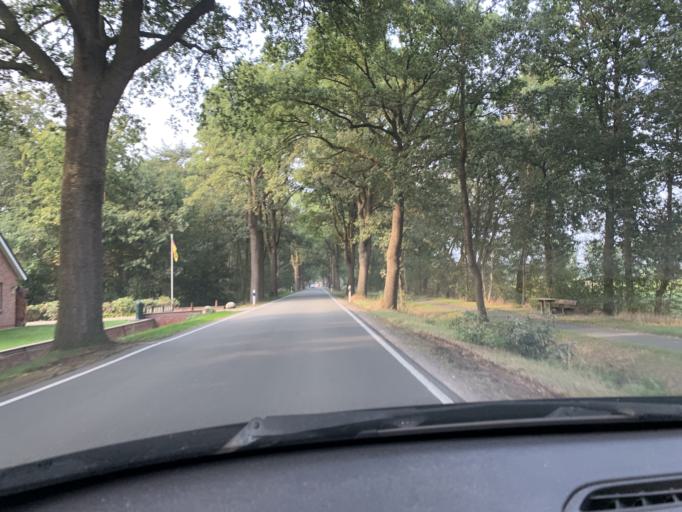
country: DE
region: Lower Saxony
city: Apen
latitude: 53.2050
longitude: 7.7941
